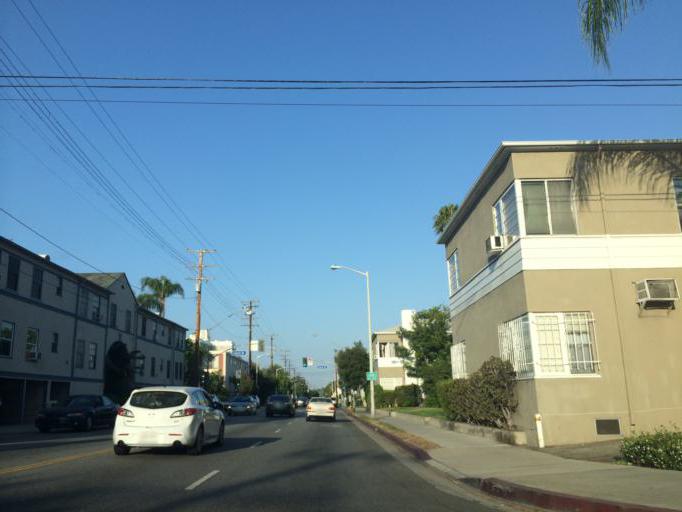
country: US
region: California
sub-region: Los Angeles County
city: West Hollywood
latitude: 34.0944
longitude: -118.3653
